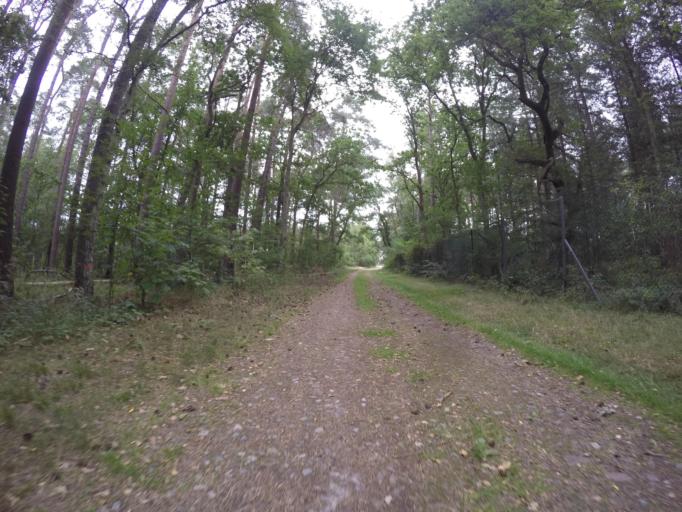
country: DE
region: Lower Saxony
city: Bleckede
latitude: 53.2791
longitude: 10.7145
